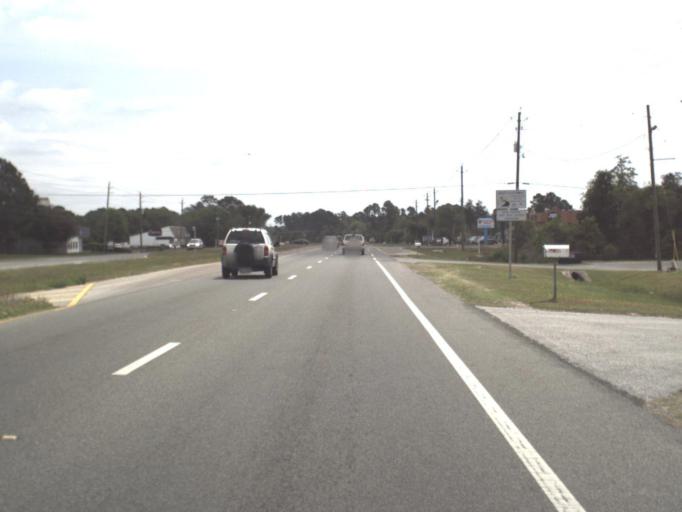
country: US
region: Florida
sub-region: Escambia County
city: Myrtle Grove
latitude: 30.3983
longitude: -87.3071
